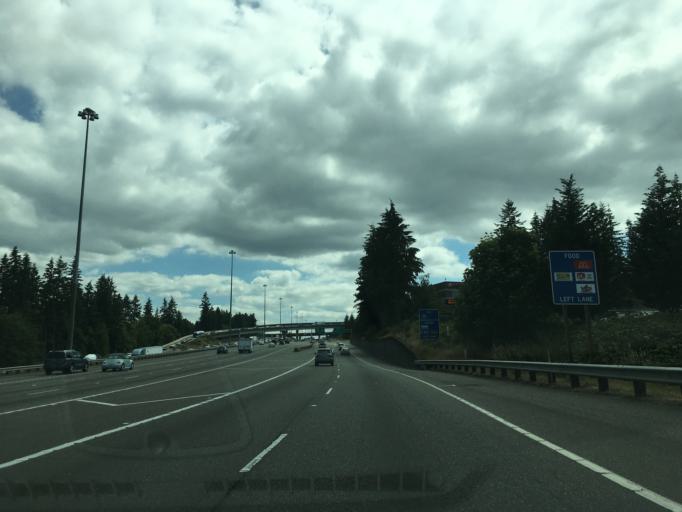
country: US
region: Washington
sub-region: Snohomish County
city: Everett
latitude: 47.9255
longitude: -122.2041
